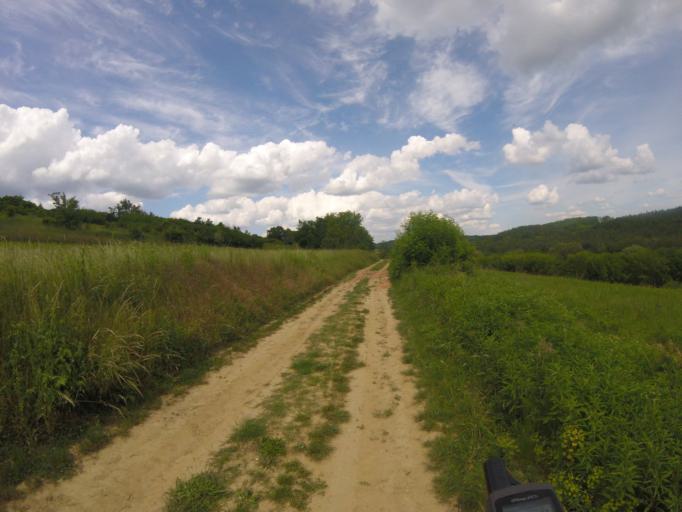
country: HU
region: Zala
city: Zalaszentgrot
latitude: 46.8876
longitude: 17.0440
